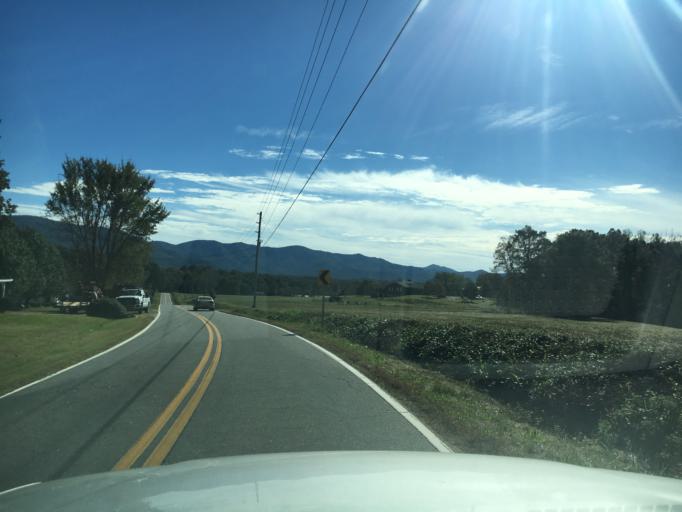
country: US
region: North Carolina
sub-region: Burke County
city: Salem
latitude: 35.7001
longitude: -81.7370
